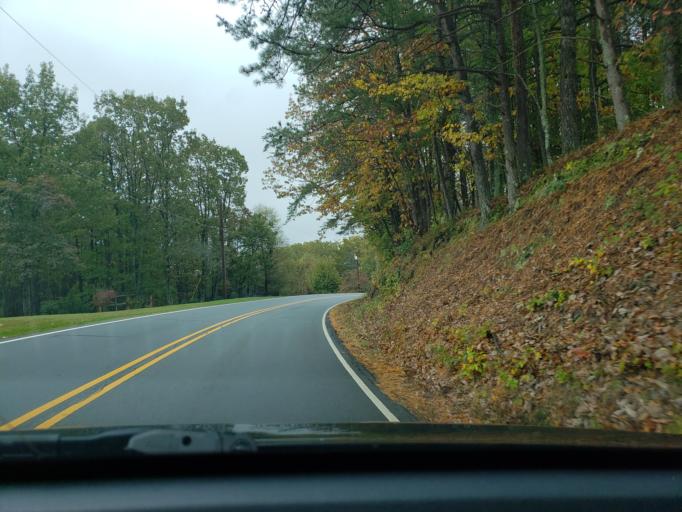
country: US
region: North Carolina
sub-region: Stokes County
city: Danbury
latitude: 36.4155
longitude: -80.2423
